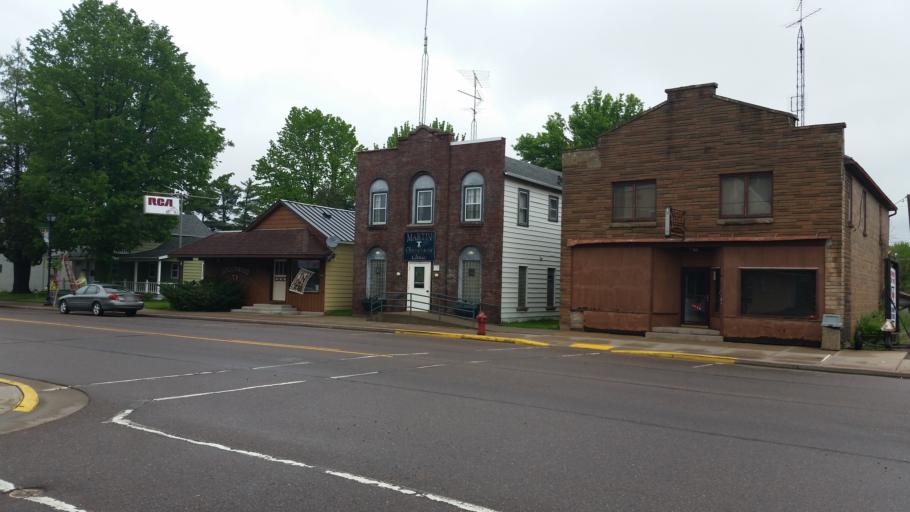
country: US
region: Wisconsin
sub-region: Clark County
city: Greenwood
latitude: 44.7606
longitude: -90.5951
